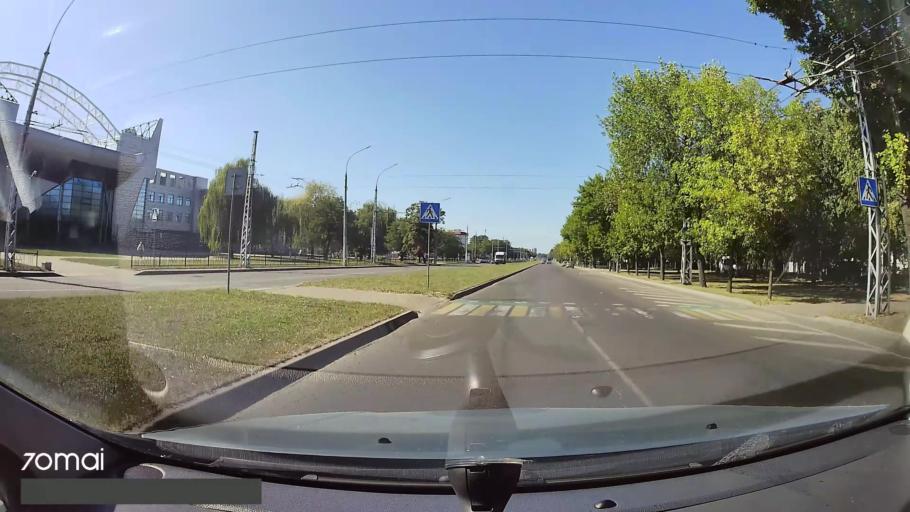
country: BY
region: Brest
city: Brest
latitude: 52.1150
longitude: 23.7782
